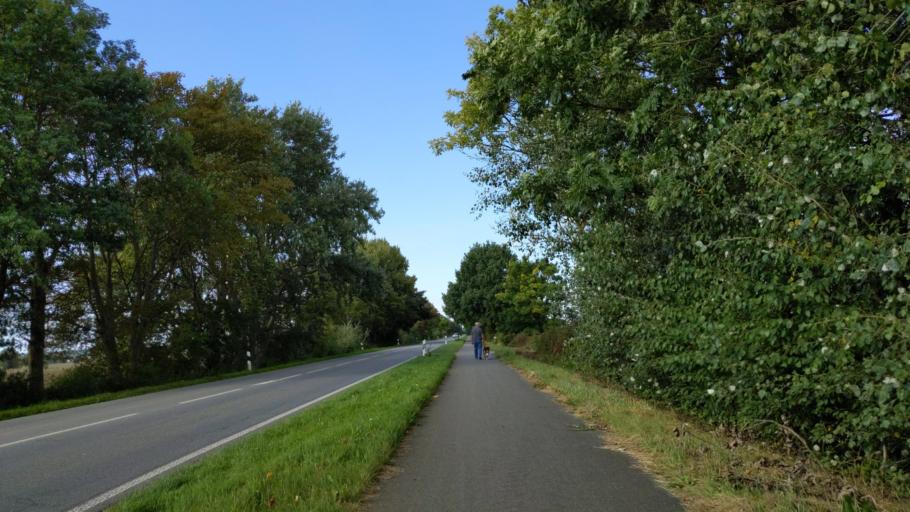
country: DE
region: Schleswig-Holstein
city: Stockelsdorf
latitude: 53.9374
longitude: 10.6320
